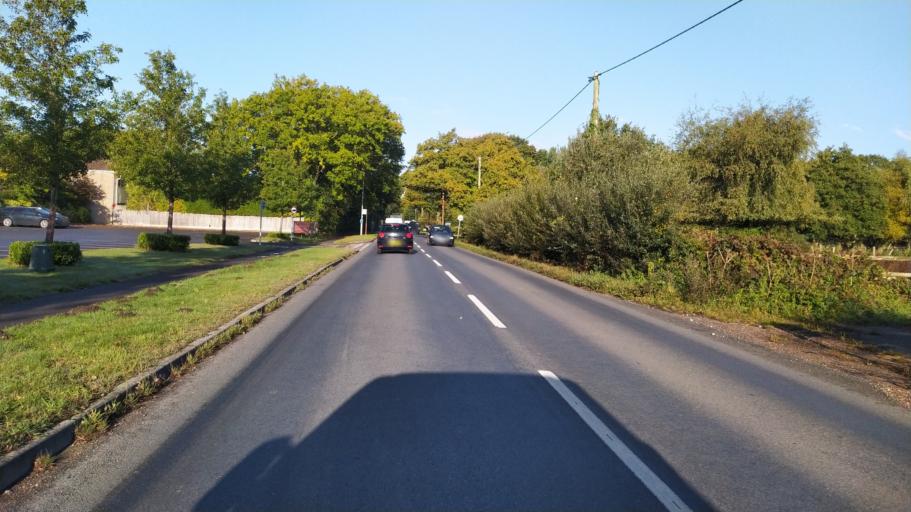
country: GB
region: England
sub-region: Dorset
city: Three Legged Cross
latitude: 50.8482
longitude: -1.8781
